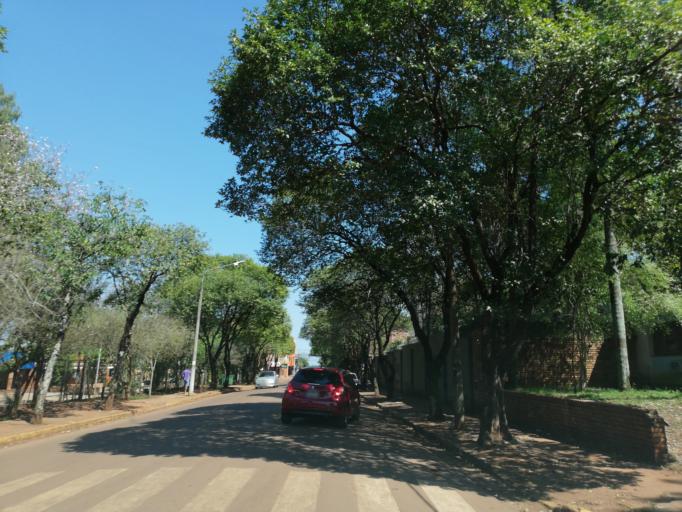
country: AR
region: Misiones
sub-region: Departamento de Eldorado
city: Eldorado
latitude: -26.4109
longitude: -54.6077
